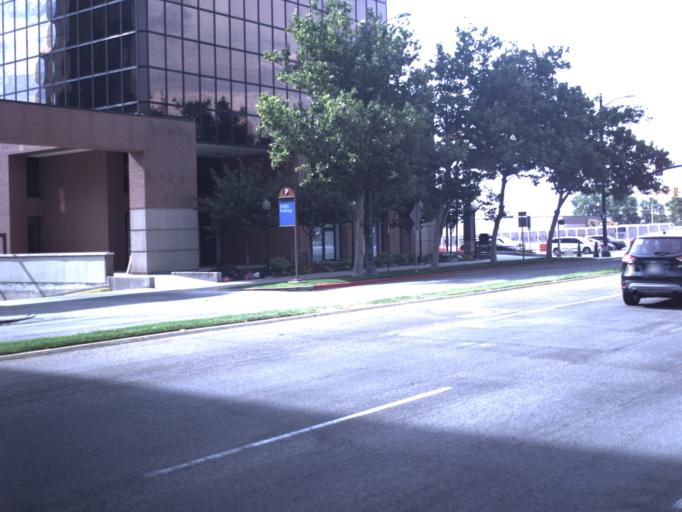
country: US
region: Utah
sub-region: Salt Lake County
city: Salt Lake City
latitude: 40.7707
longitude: -111.8996
